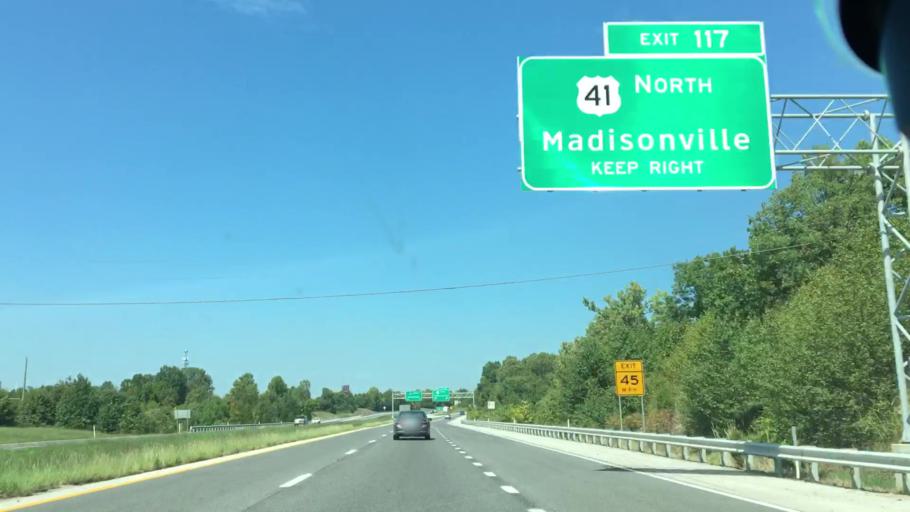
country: US
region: Kentucky
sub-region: Hopkins County
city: Madisonville
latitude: 37.3555
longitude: -87.4879
